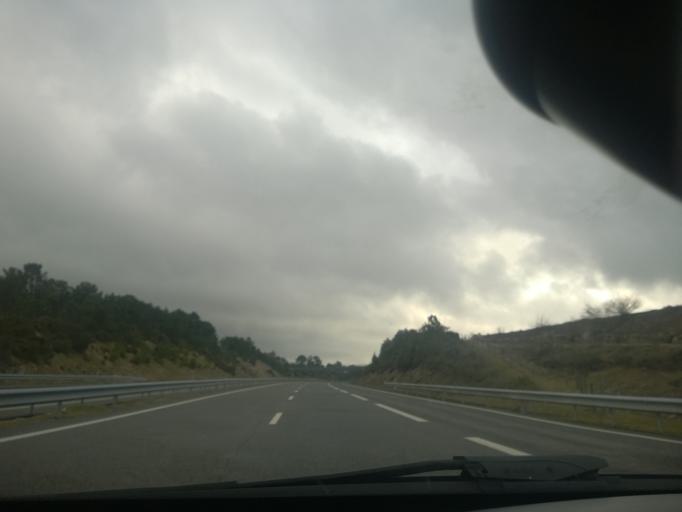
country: PT
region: Vila Real
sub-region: Boticas
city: Boticas
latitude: 41.6063
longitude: -7.6256
